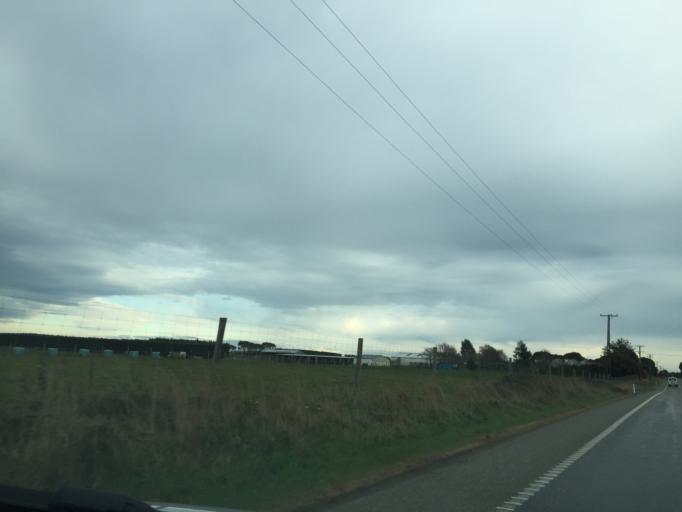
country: NZ
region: Southland
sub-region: Invercargill City
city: Invercargill
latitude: -46.3133
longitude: 168.6751
